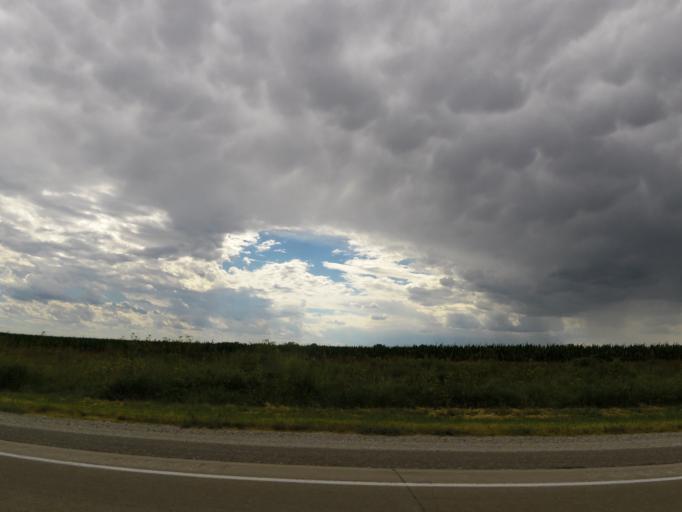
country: US
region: Iowa
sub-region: Henry County
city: Mount Pleasant
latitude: 41.0479
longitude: -91.5448
